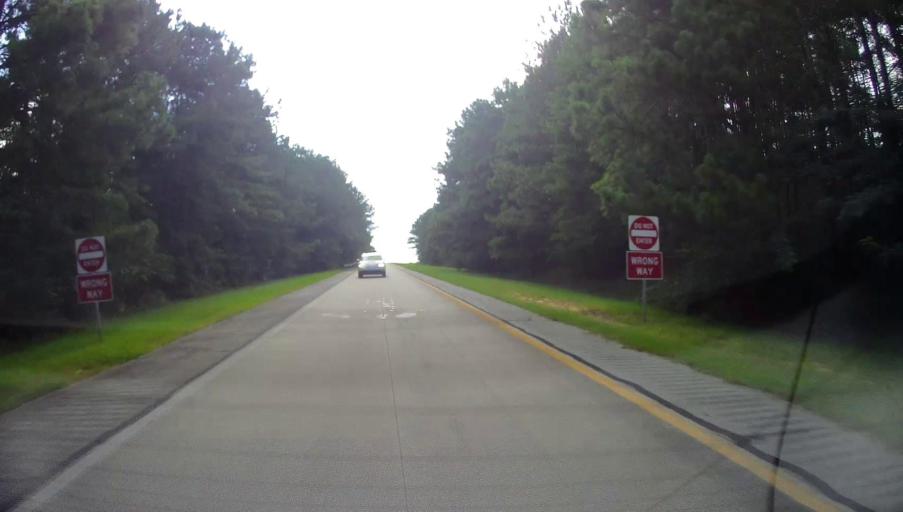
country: US
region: Alabama
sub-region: Russell County
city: Phenix City
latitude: 32.5519
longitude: -84.9301
